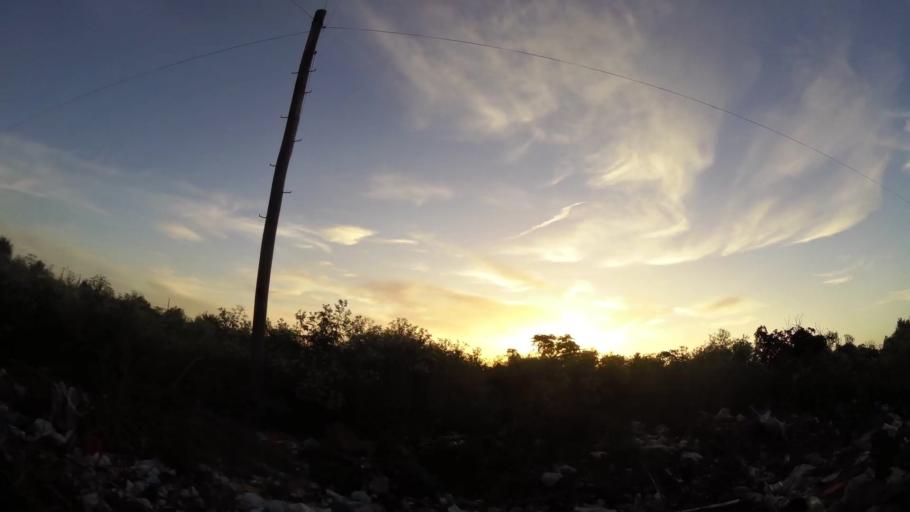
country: AR
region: Buenos Aires
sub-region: Partido de Quilmes
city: Quilmes
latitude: -34.7865
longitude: -58.2250
